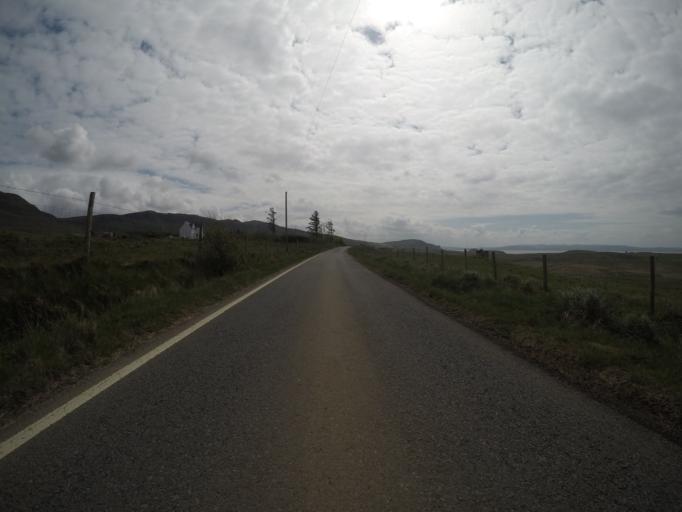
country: GB
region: Scotland
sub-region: Highland
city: Portree
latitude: 57.6276
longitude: -6.3777
